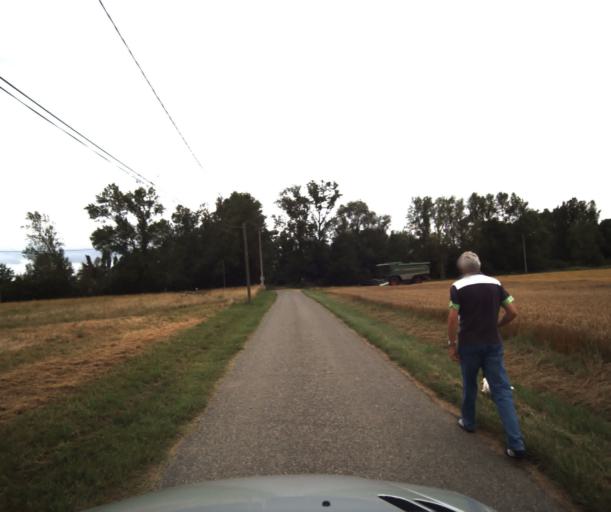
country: FR
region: Midi-Pyrenees
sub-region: Departement de la Haute-Garonne
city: Lacroix-Falgarde
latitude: 43.4754
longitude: 1.4129
